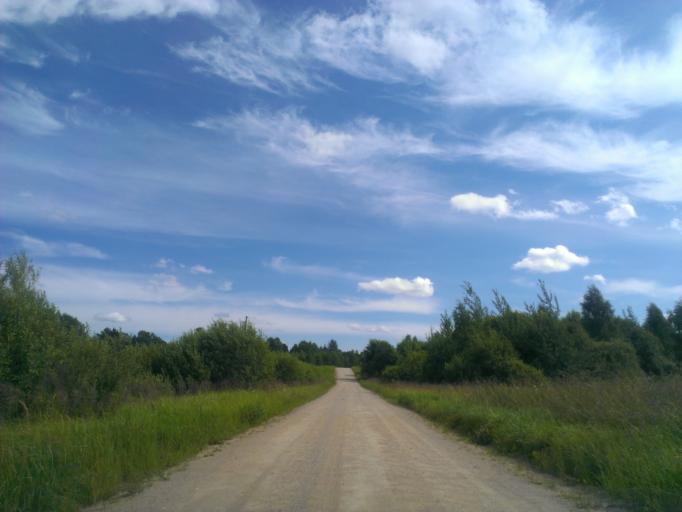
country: LV
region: Ligatne
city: Ligatne
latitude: 57.2201
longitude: 25.0080
